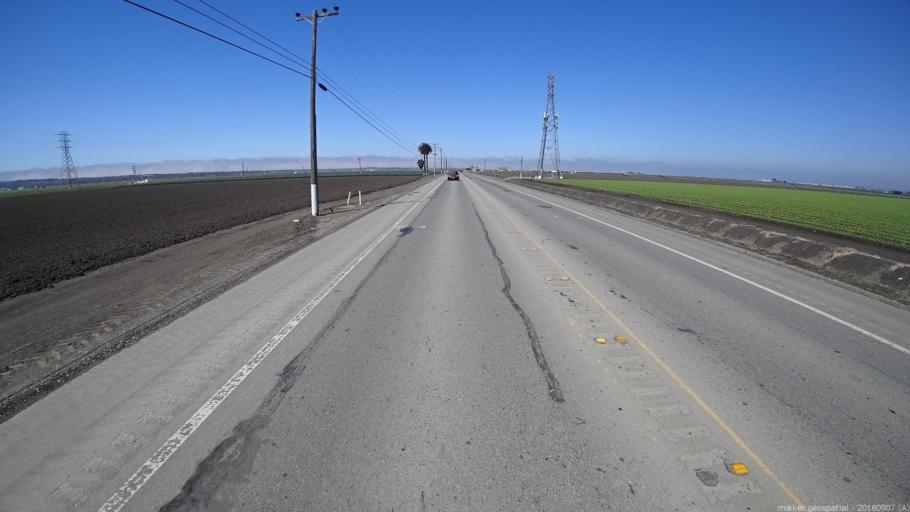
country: US
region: California
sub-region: Monterey County
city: Boronda
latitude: 36.6735
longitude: -121.6971
